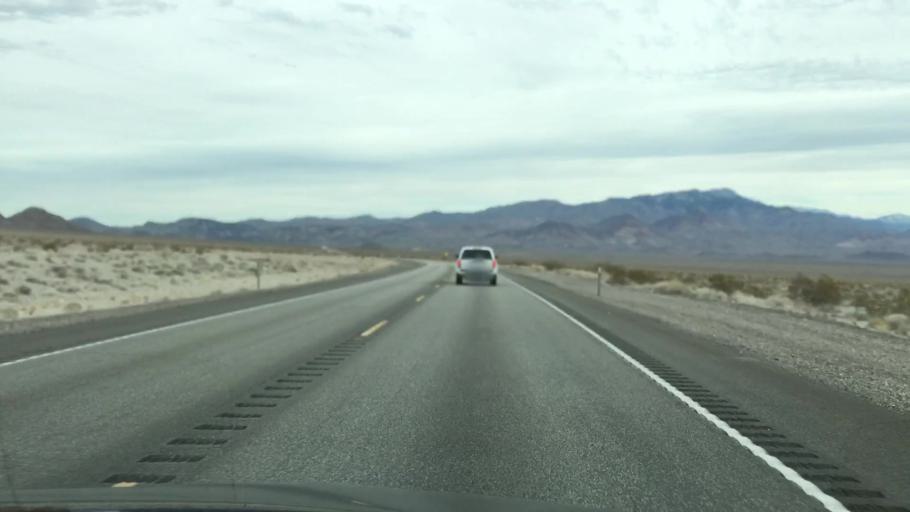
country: US
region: Nevada
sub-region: Nye County
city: Pahrump
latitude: 36.5741
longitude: -116.1861
